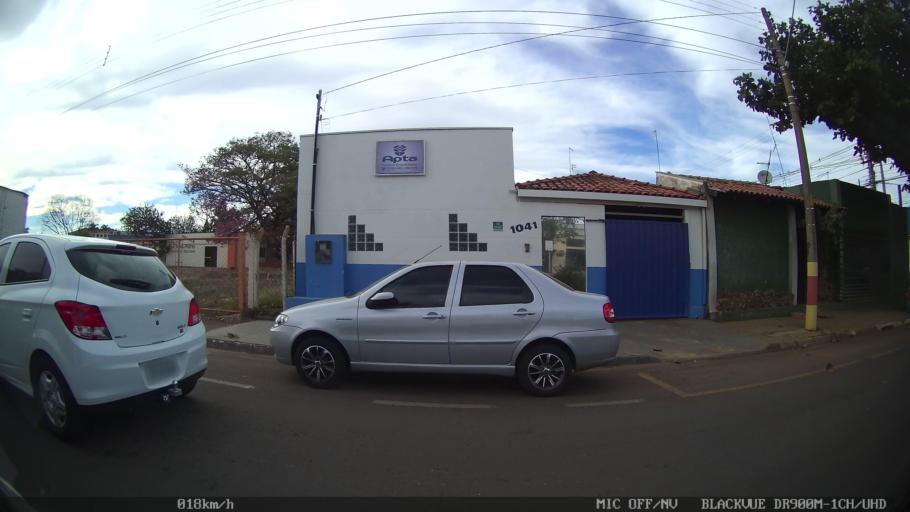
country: BR
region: Sao Paulo
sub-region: Catanduva
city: Catanduva
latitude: -21.1288
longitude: -48.9842
